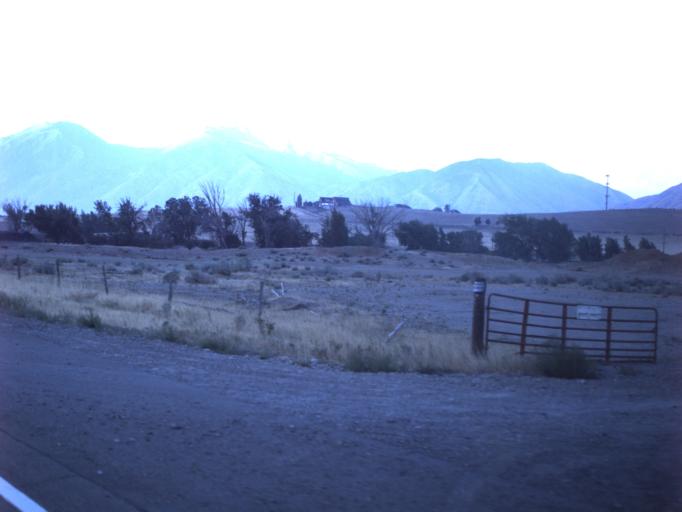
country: US
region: Utah
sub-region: Utah County
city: Mapleton
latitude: 40.0935
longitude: -111.5912
